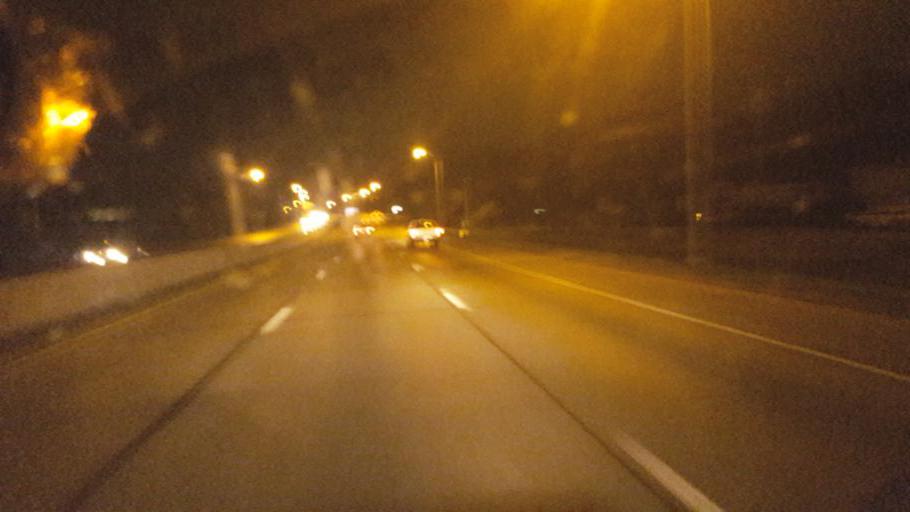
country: US
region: Indiana
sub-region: Marion County
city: Indianapolis
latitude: 39.7561
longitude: -86.2012
